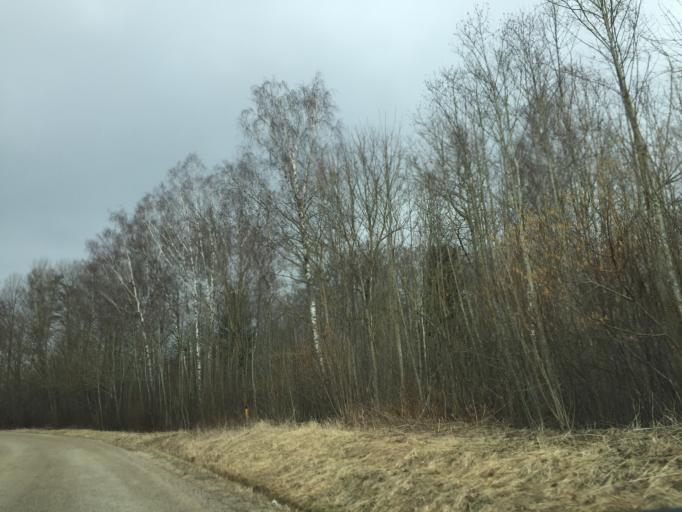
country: LV
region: Ilukste
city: Ilukste
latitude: 56.0206
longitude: 26.2359
